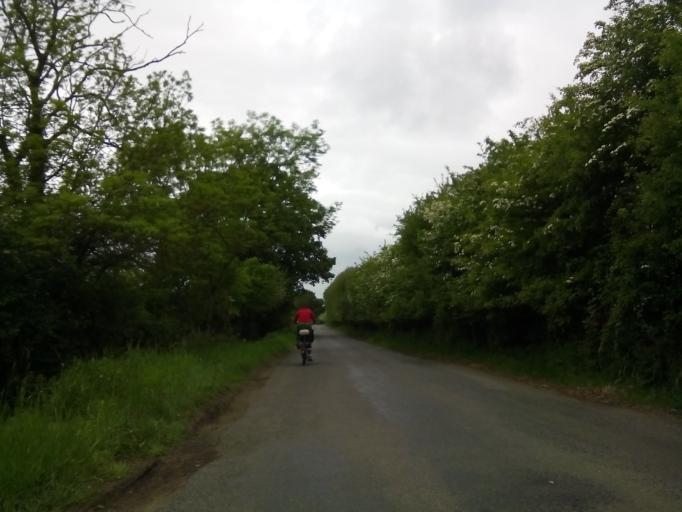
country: GB
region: England
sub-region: Northamptonshire
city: Oundle
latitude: 52.5203
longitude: -0.5427
